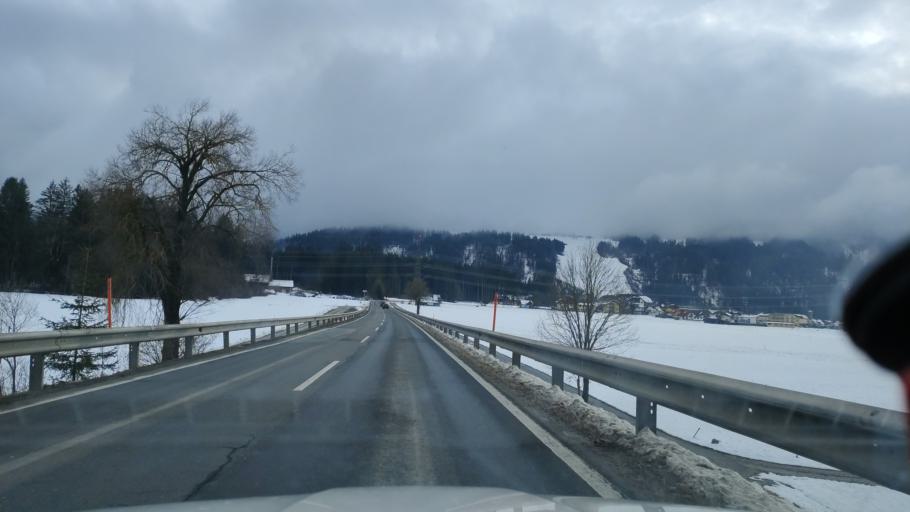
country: AT
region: Carinthia
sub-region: Politischer Bezirk Hermagor
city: Hermagor
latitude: 46.6211
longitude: 13.2871
